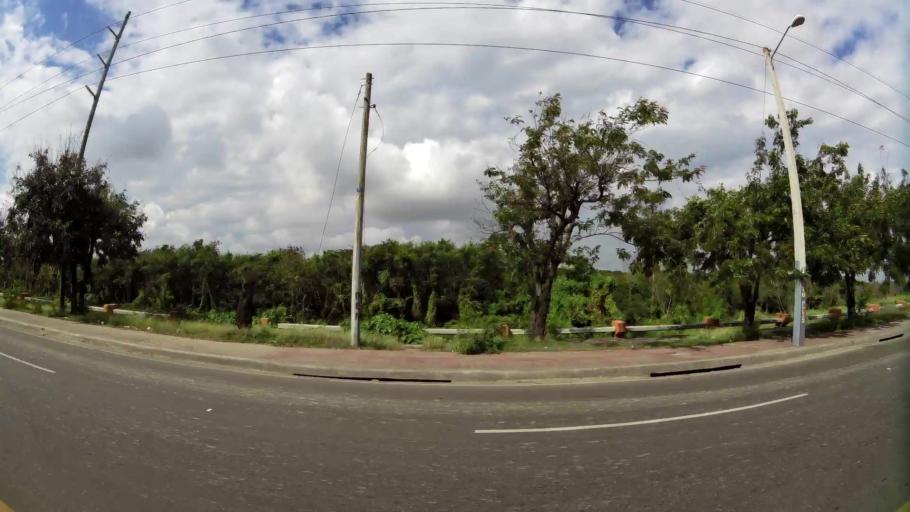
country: DO
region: Santiago
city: Santiago de los Caballeros
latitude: 19.4653
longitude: -70.7132
